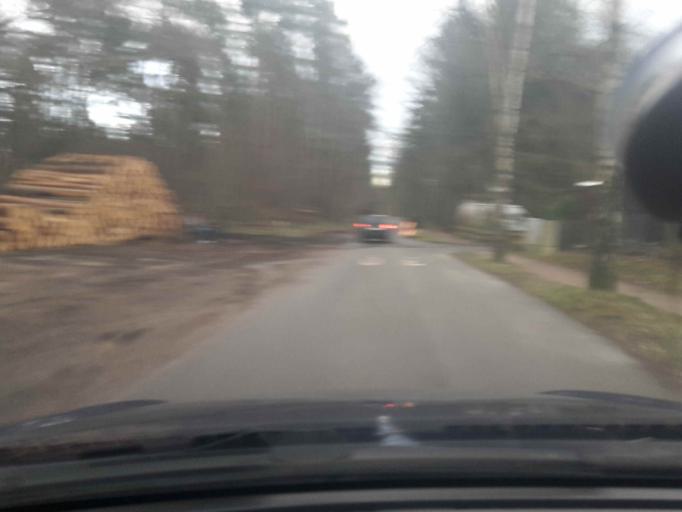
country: DE
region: Lower Saxony
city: Buchholz in der Nordheide
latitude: 53.2856
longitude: 9.8815
